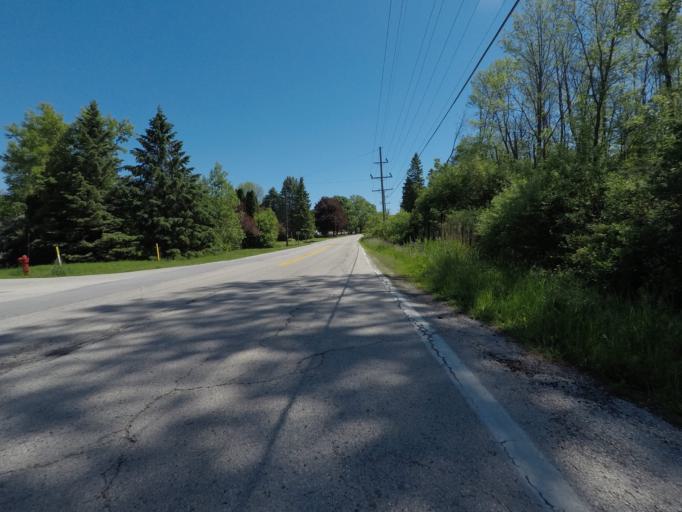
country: US
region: Wisconsin
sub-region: Sheboygan County
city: Kohler
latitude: 43.7507
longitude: -87.7577
